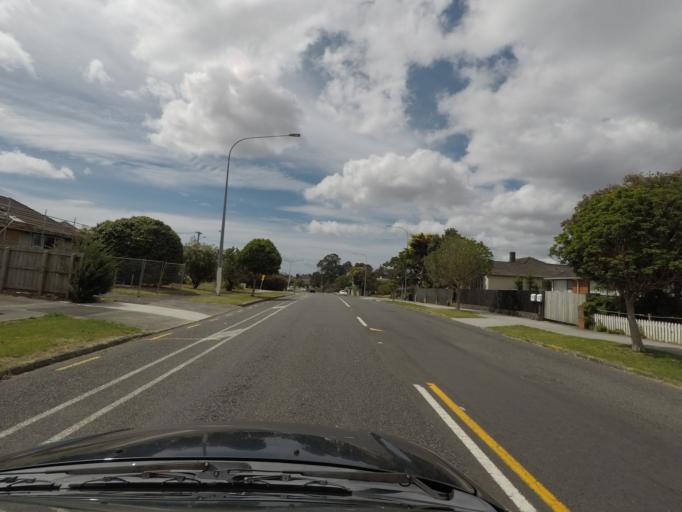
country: NZ
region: Auckland
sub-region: Auckland
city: Auckland
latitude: -36.9021
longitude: 174.7300
